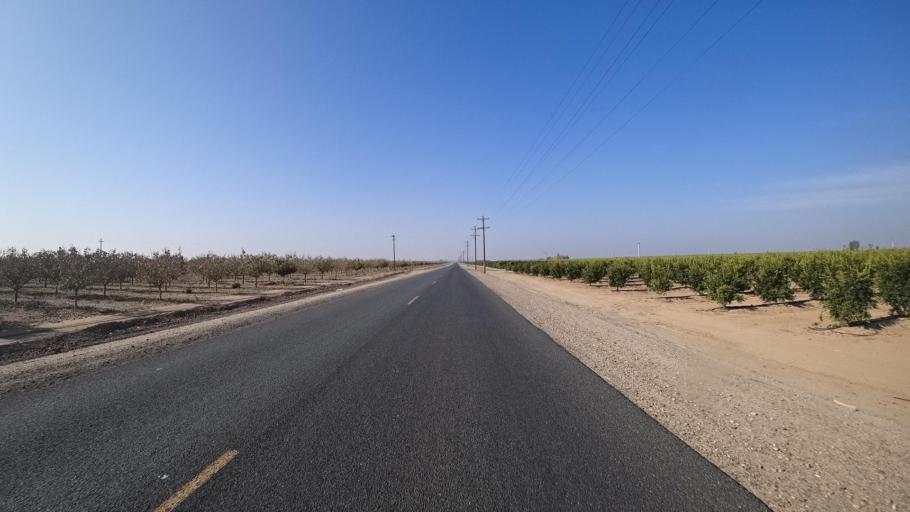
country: US
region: California
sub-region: Kern County
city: McFarland
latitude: 35.6021
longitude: -119.1766
